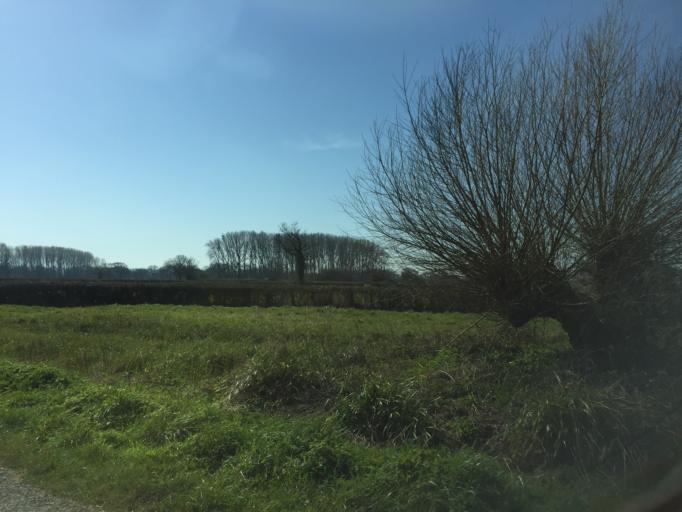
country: GB
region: England
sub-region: South Gloucestershire
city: Hill
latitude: 51.6499
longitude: -2.5173
